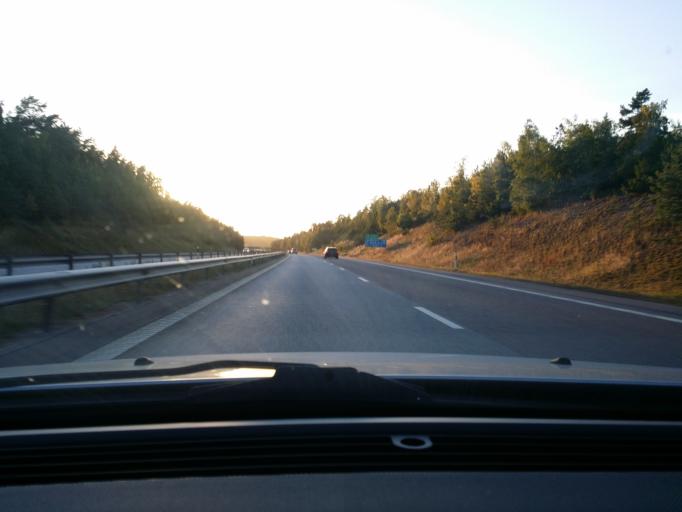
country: SE
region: Uppsala
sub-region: Habo Kommun
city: Balsta
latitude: 59.5804
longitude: 17.5306
